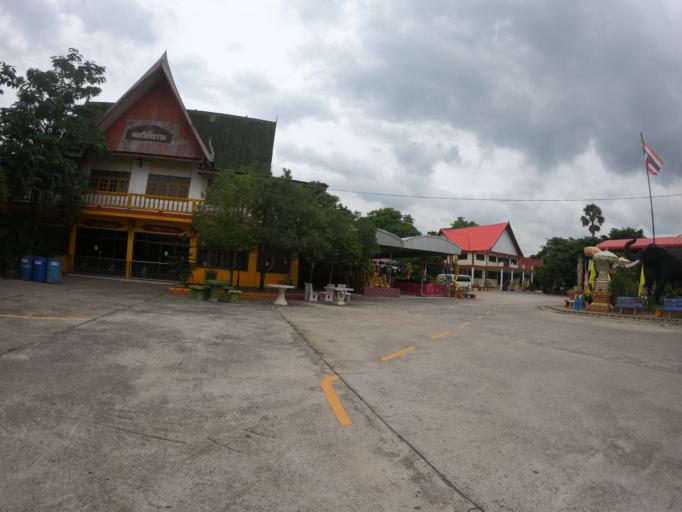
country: TH
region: Pathum Thani
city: Nong Suea
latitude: 14.0370
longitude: 100.8675
